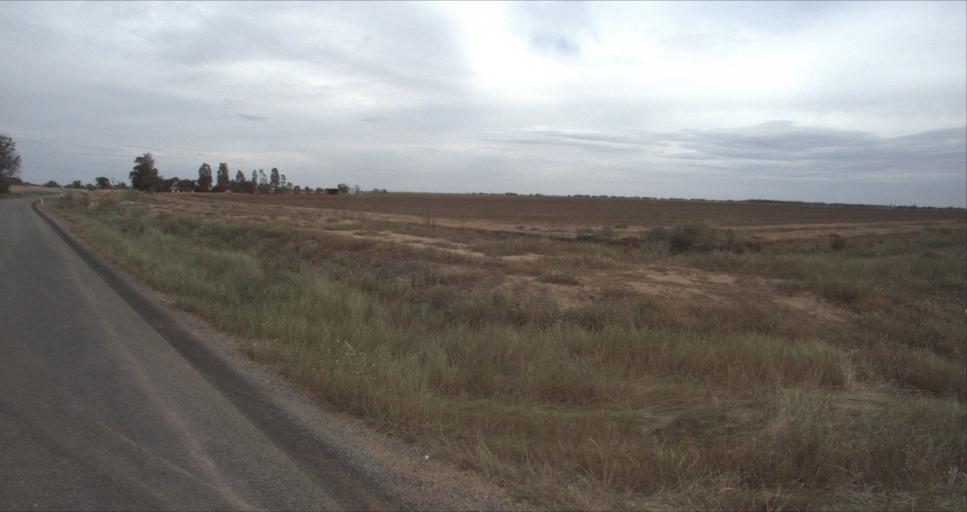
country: AU
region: New South Wales
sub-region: Leeton
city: Leeton
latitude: -34.4282
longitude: 146.3779
